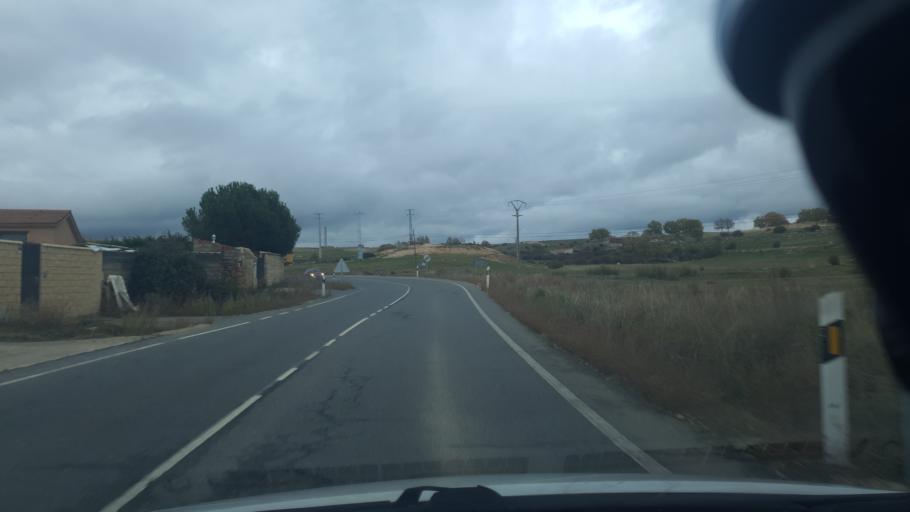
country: ES
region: Castille and Leon
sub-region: Provincia de Segovia
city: La Lastrilla
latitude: 40.9757
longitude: -4.0862
